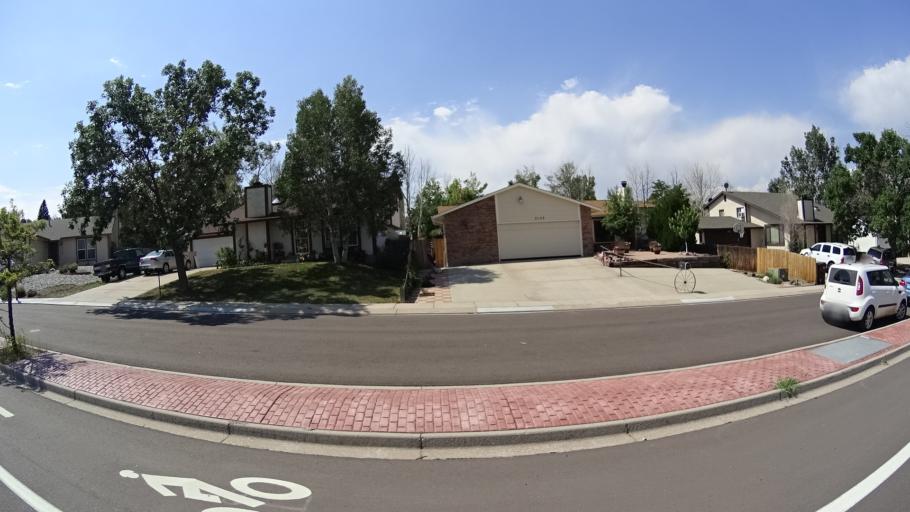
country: US
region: Colorado
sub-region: El Paso County
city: Cimarron Hills
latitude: 38.9251
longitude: -104.7698
